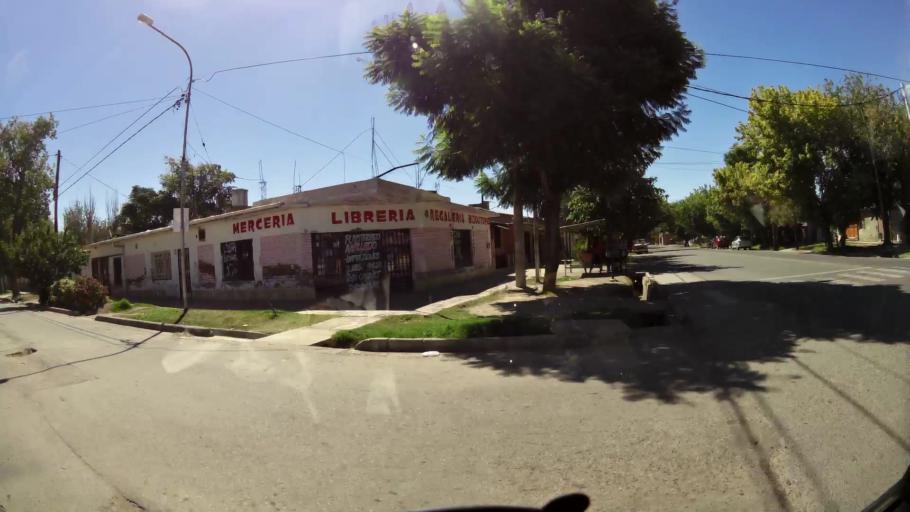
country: AR
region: Mendoza
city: Las Heras
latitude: -32.8340
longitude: -68.8406
